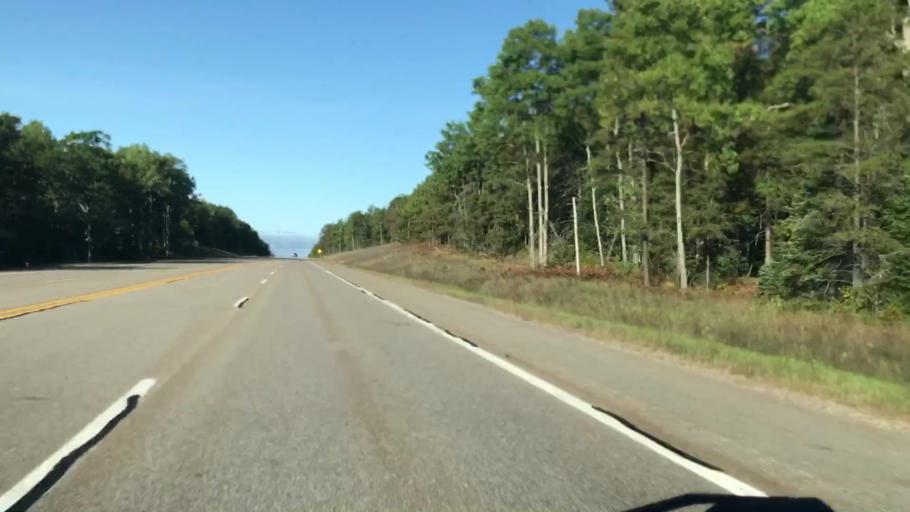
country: US
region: Michigan
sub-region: Chippewa County
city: Sault Ste. Marie
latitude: 46.3646
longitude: -84.7637
